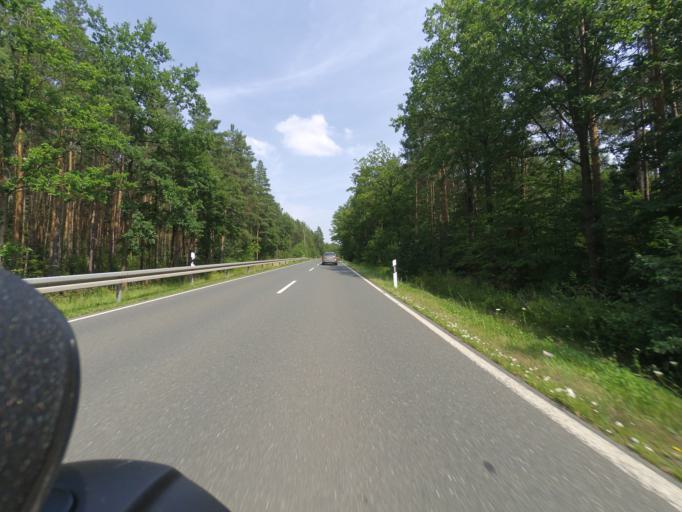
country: DE
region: Thuringia
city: Rauda
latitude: 50.9263
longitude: 11.9551
